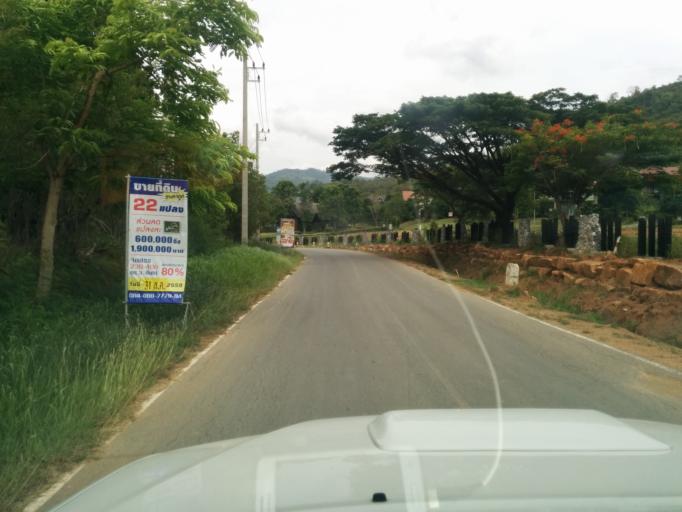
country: TH
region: Sara Buri
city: Muak Lek
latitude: 14.5611
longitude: 101.2533
